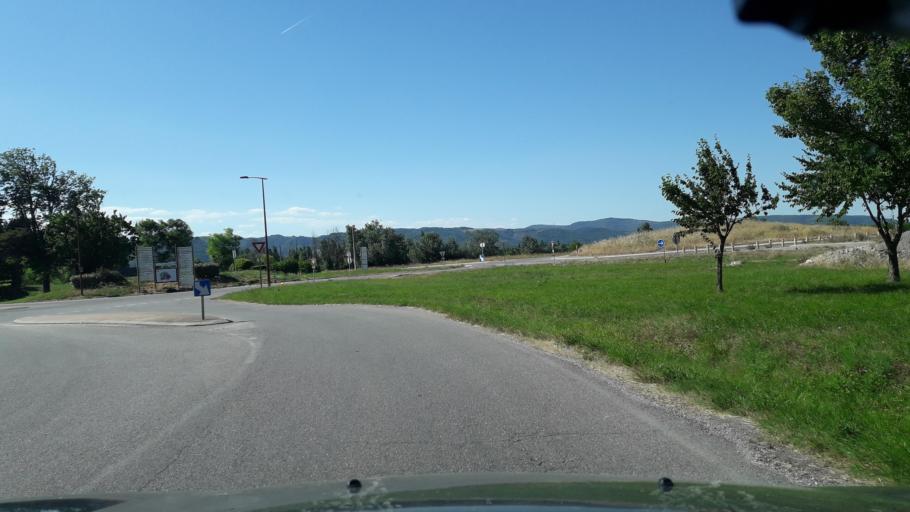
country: FR
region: Rhone-Alpes
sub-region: Departement de la Drome
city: Loriol-sur-Drome
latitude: 44.7541
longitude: 4.7992
